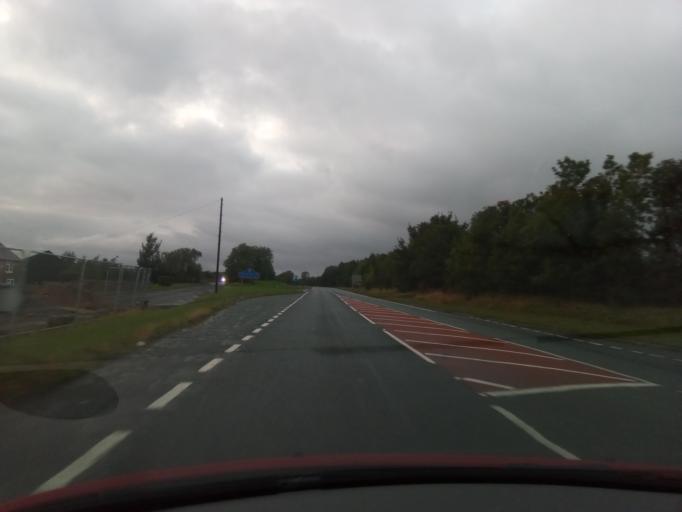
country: GB
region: England
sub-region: Darlington
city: Summerhouse
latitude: 54.6085
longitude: -1.6814
